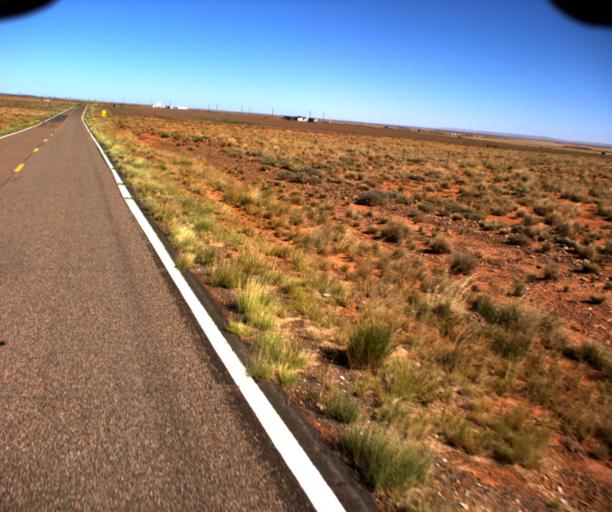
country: US
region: Arizona
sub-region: Coconino County
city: LeChee
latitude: 35.1334
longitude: -110.8832
